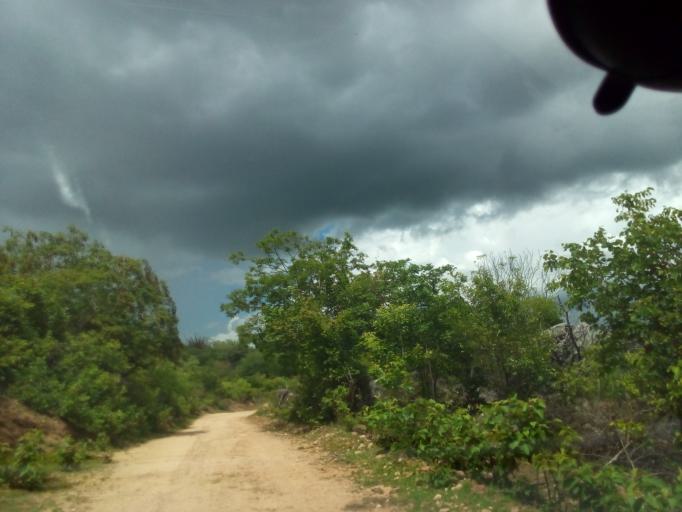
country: BR
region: Rio Grande do Norte
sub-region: Sao Tome
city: Sao Tome
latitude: -5.9520
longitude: -35.9186
